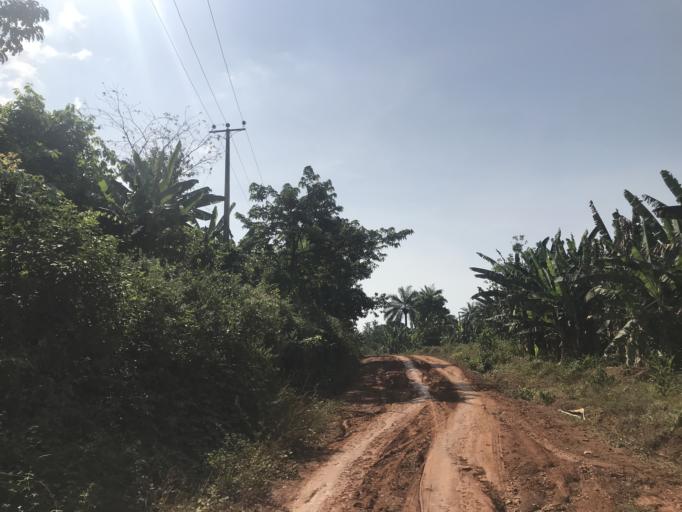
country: NG
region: Osun
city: Osu
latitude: 7.6339
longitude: 4.6688
